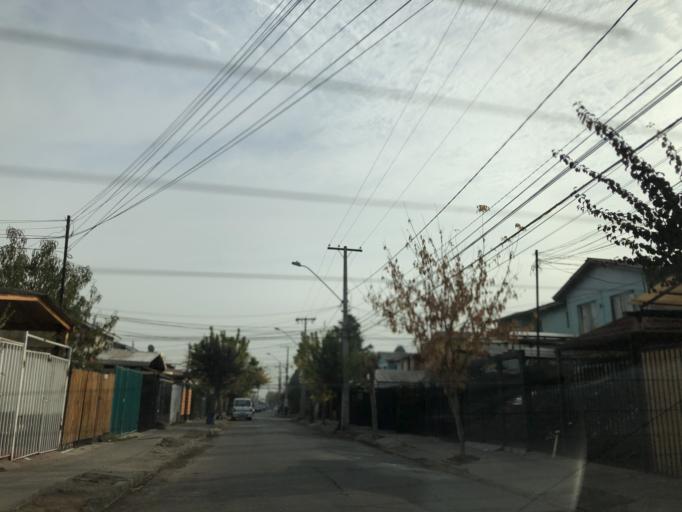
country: CL
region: Santiago Metropolitan
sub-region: Provincia de Cordillera
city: Puente Alto
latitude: -33.5852
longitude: -70.5543
